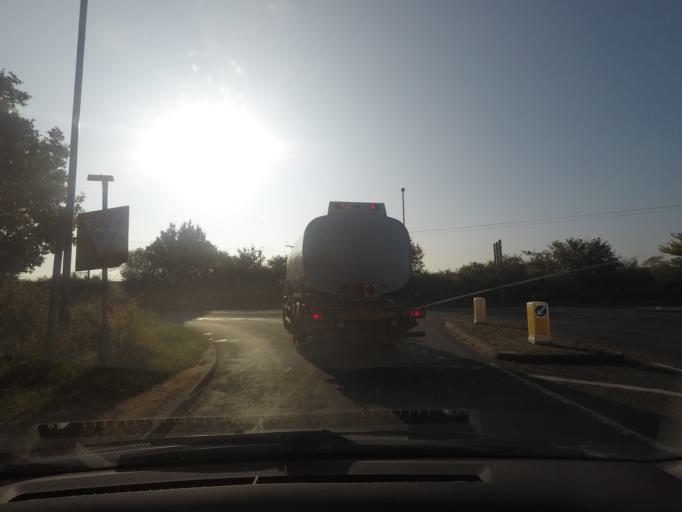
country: GB
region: England
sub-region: City and Borough of Leeds
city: Walton
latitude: 54.0026
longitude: -1.3038
